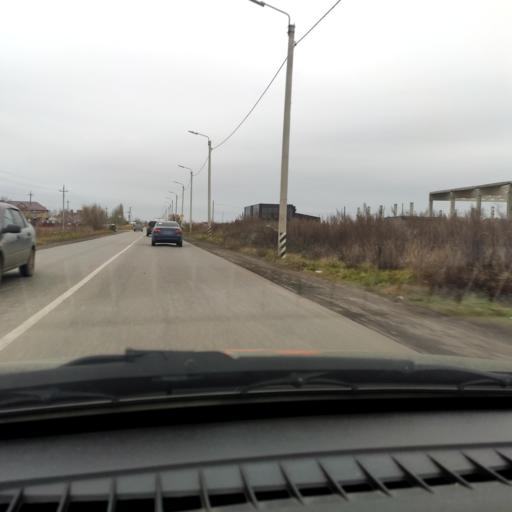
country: RU
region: Samara
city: Podstepki
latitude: 53.5222
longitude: 49.1727
